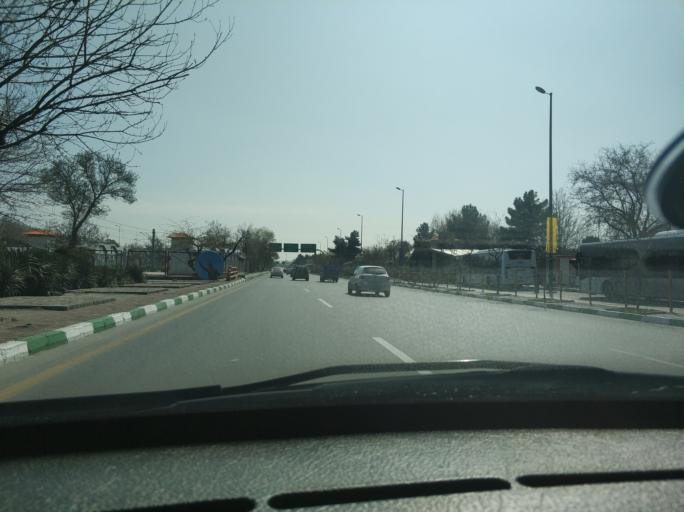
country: IR
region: Razavi Khorasan
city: Mashhad
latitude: 36.3177
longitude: 59.5320
